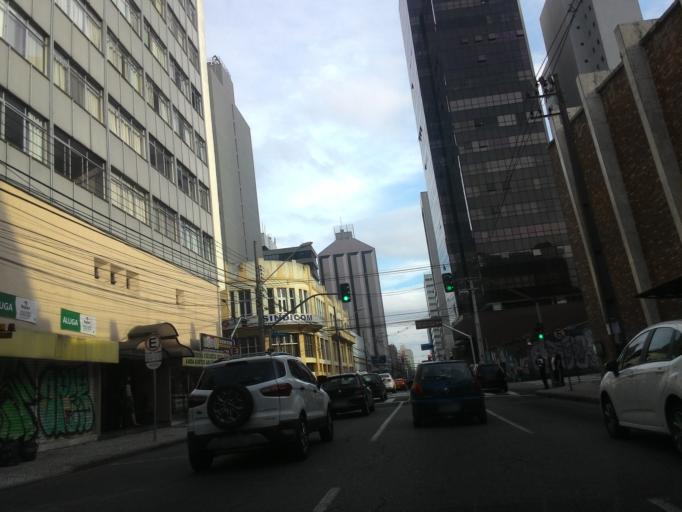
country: BR
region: Parana
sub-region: Curitiba
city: Curitiba
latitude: -25.4280
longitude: -49.2645
